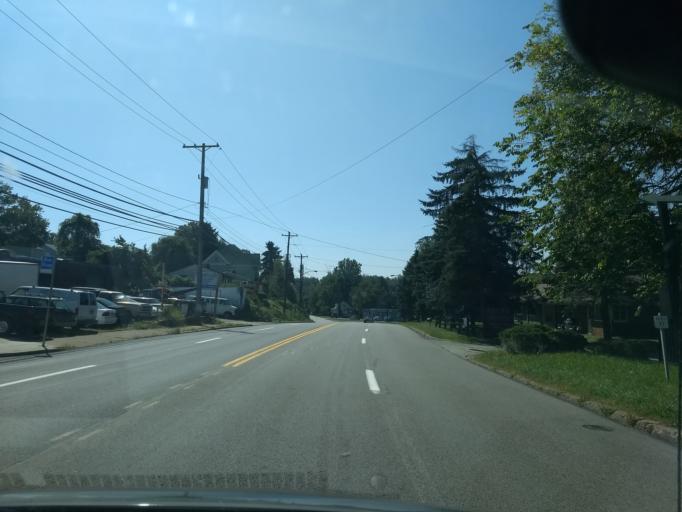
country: US
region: Pennsylvania
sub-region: Allegheny County
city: North Versailles
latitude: 40.3715
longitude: -79.8283
